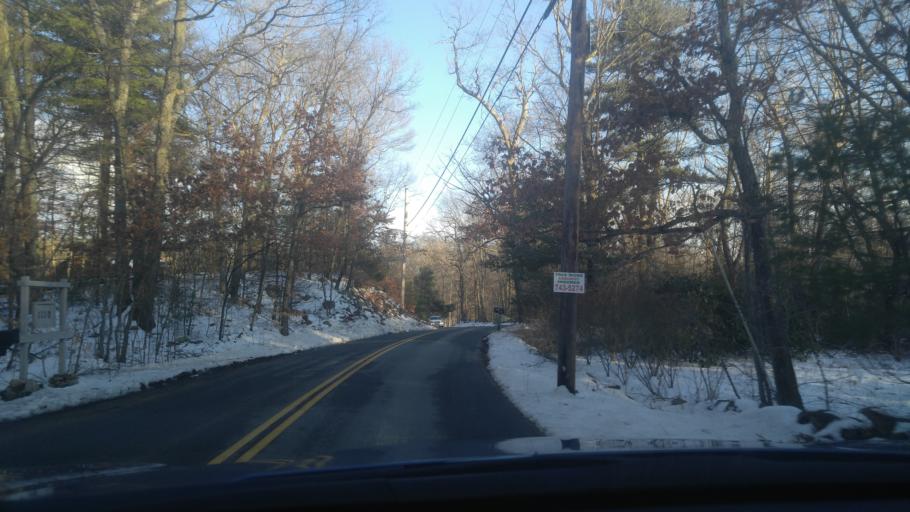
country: US
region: Rhode Island
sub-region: Kent County
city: Coventry
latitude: 41.7204
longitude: -71.6819
